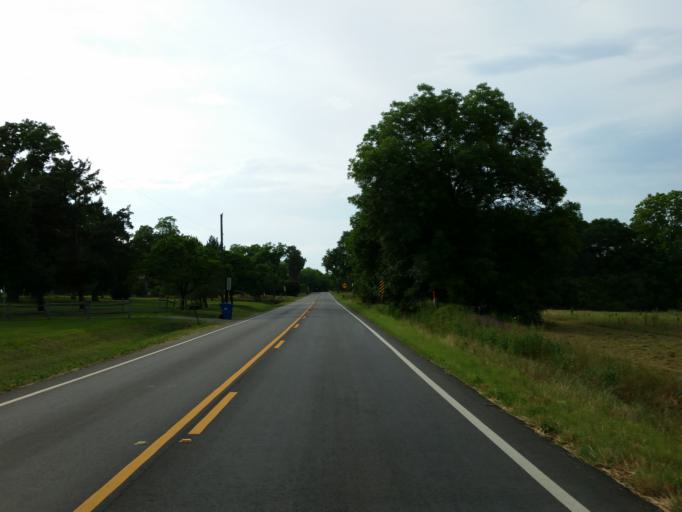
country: US
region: Georgia
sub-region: Turner County
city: Ashburn
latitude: 31.7737
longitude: -83.6915
